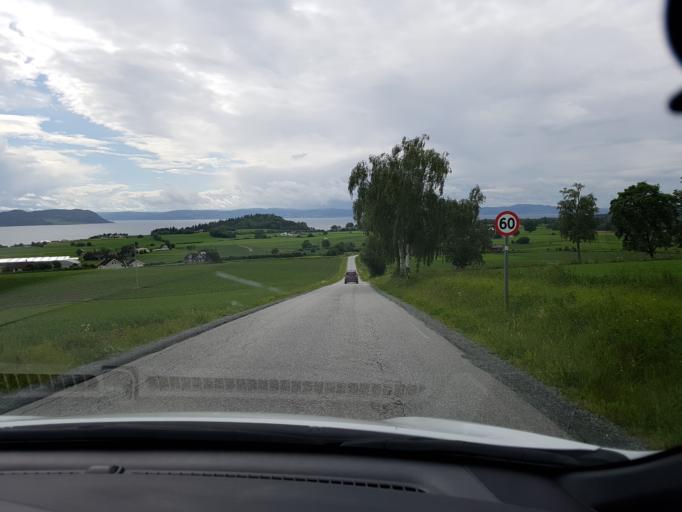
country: NO
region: Nord-Trondelag
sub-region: Frosta
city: Frosta
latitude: 63.5783
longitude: 10.7131
